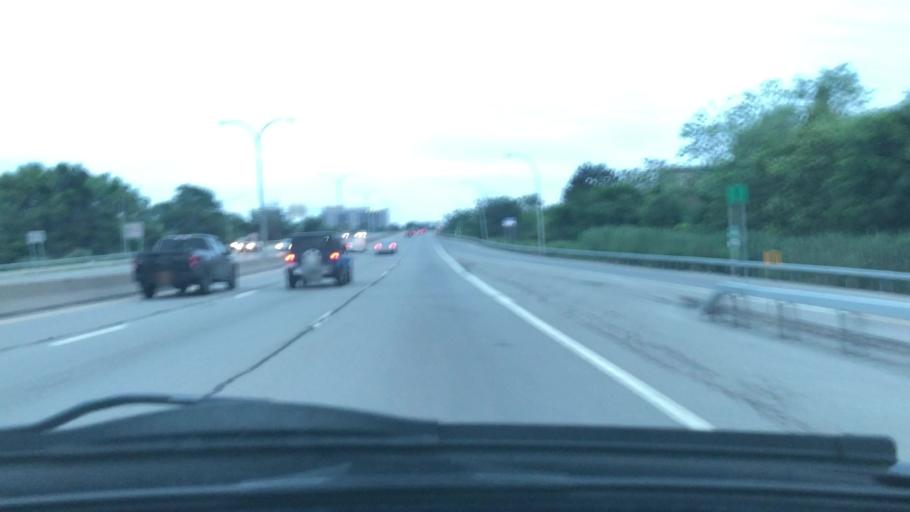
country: US
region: New York
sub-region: Erie County
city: Eggertsville
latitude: 42.9319
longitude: -78.8158
